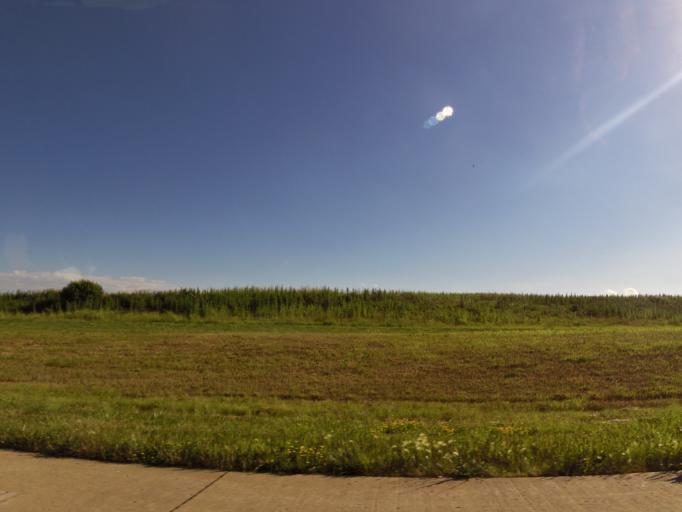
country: US
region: Missouri
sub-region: Ralls County
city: New London
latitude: 39.5369
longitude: -91.3632
